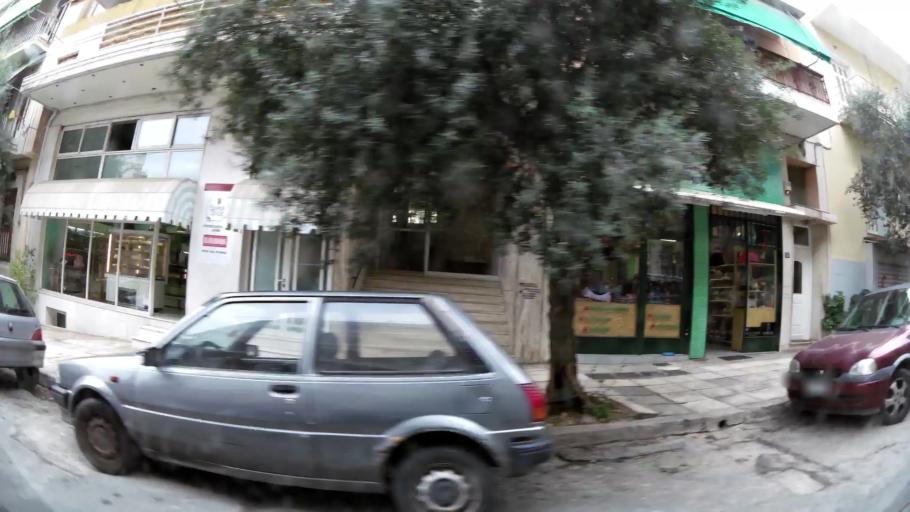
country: GR
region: Attica
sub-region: Nomarchia Athinas
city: Vyronas
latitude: 37.9651
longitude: 23.7438
